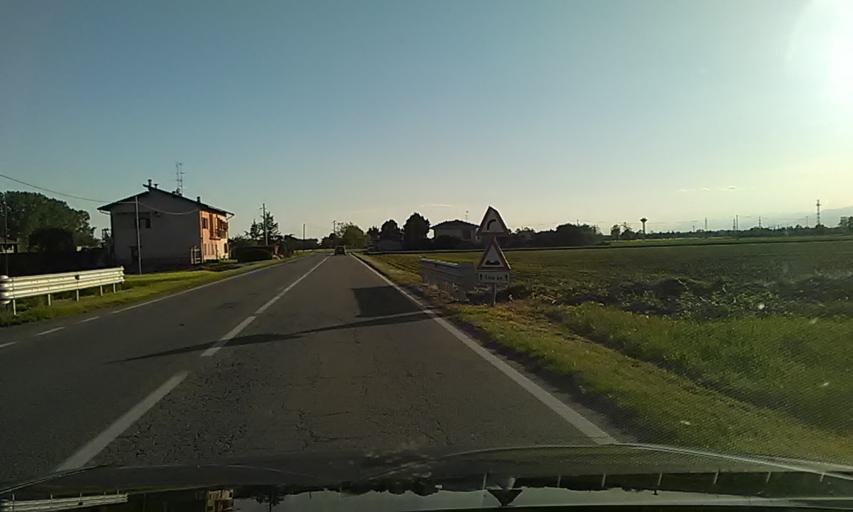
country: IT
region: Piedmont
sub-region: Provincia di Novara
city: Momo
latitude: 45.5800
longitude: 8.5739
